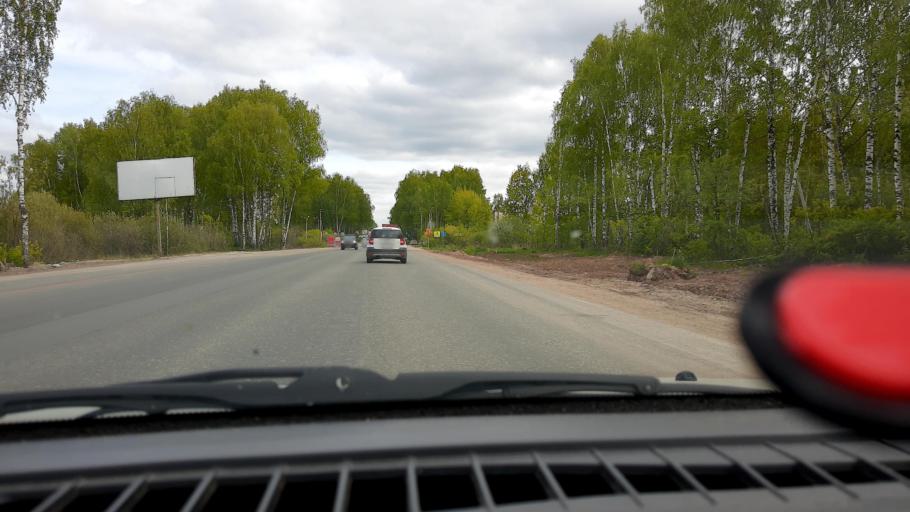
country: RU
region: Nizjnij Novgorod
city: Neklyudovo
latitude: 56.4200
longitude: 43.9975
